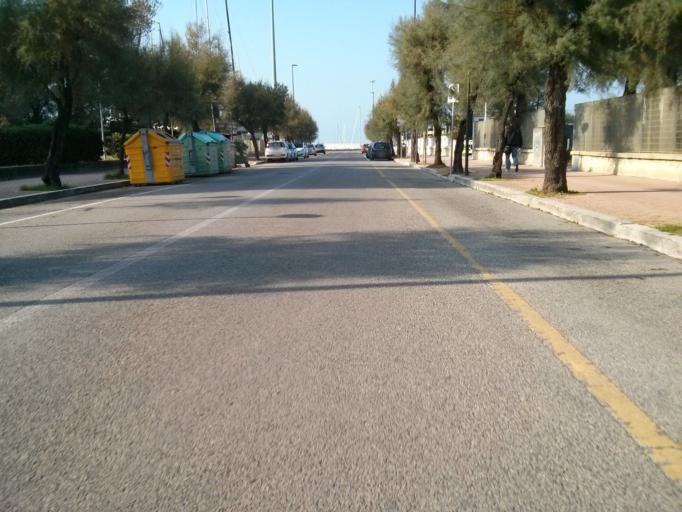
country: IT
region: The Marches
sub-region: Provincia di Pesaro e Urbino
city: Pesaro
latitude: 43.9213
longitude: 12.9074
